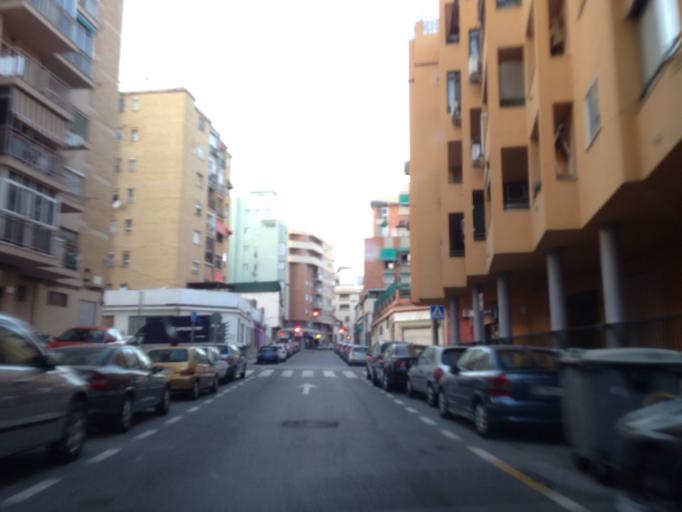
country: ES
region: Andalusia
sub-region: Provincia de Malaga
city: Malaga
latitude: 36.7269
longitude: -4.4433
